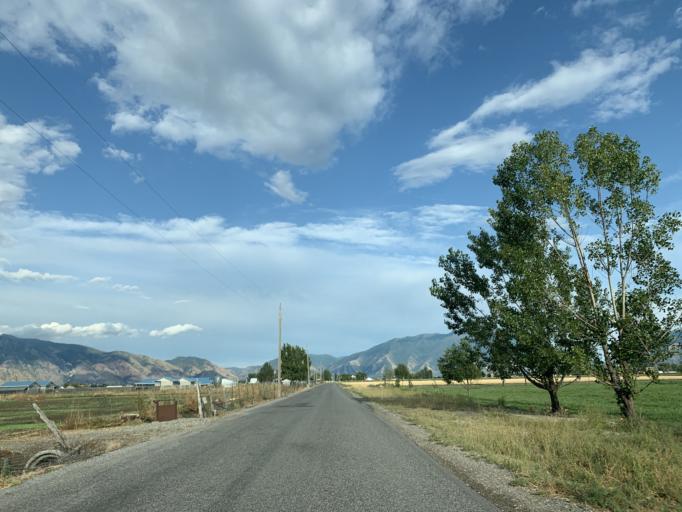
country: US
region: Utah
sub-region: Utah County
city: Benjamin
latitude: 40.1292
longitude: -111.7415
